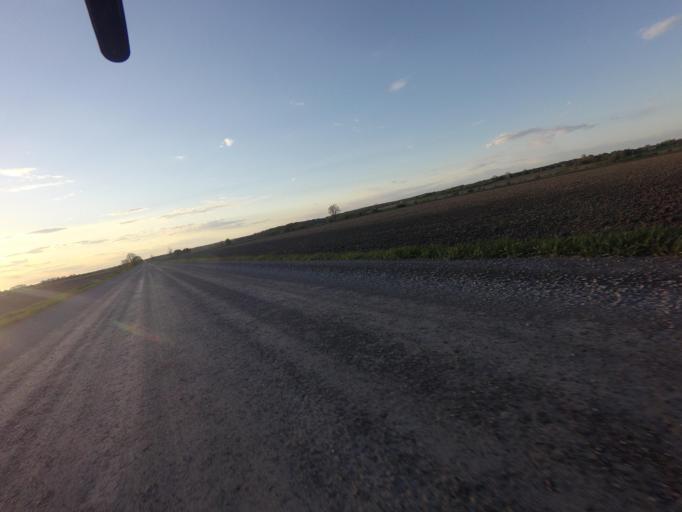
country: CA
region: Ontario
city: Arnprior
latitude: 45.3694
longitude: -76.1368
